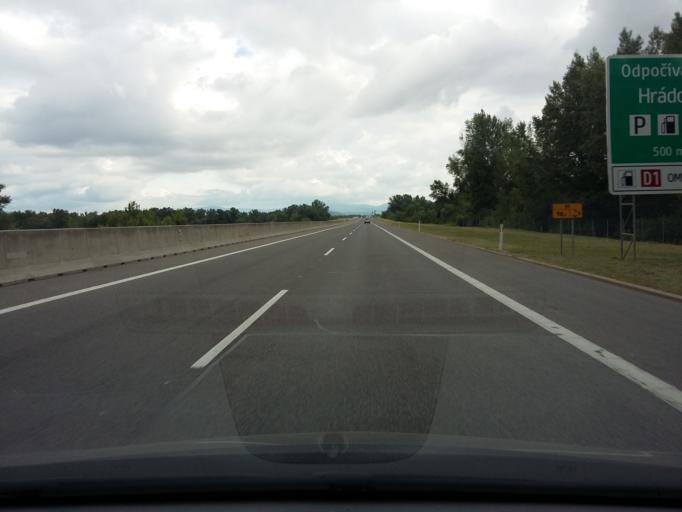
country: SK
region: Trenciansky
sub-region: Okres Nove Mesto nad Vahom
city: Nove Mesto nad Vahom
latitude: 48.6964
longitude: 17.8723
